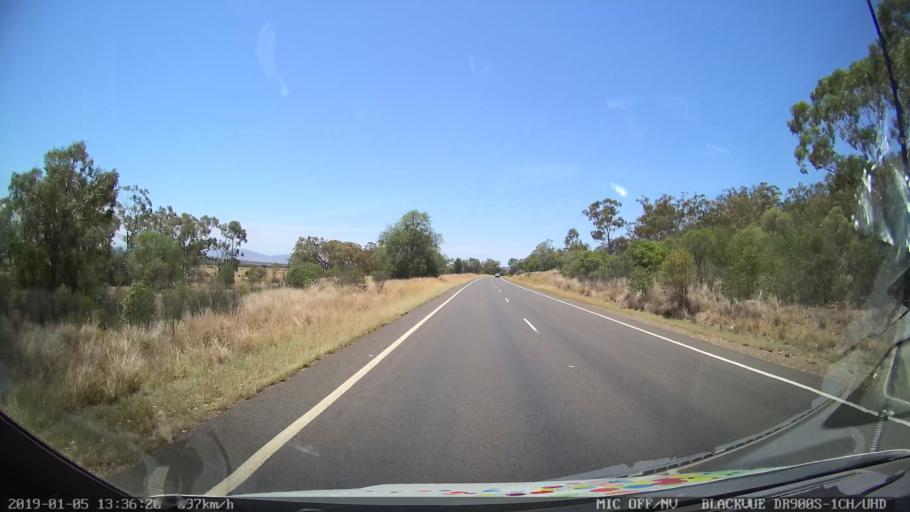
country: AU
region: New South Wales
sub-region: Gunnedah
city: Gunnedah
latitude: -30.9856
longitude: 150.1632
